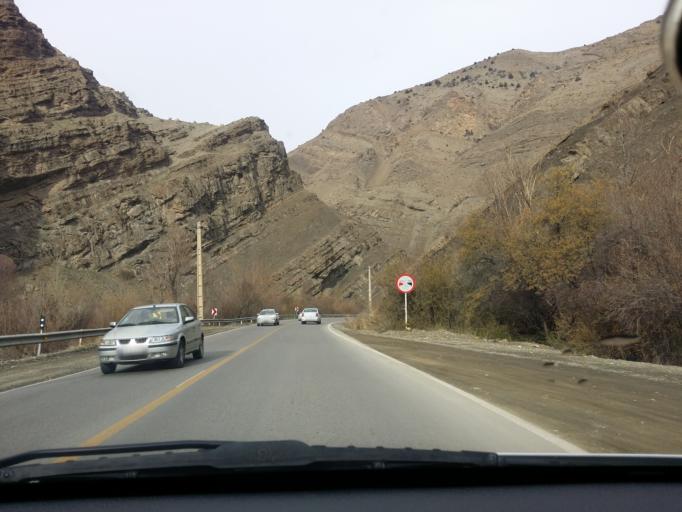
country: IR
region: Tehran
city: Tajrish
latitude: 36.0162
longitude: 51.2799
